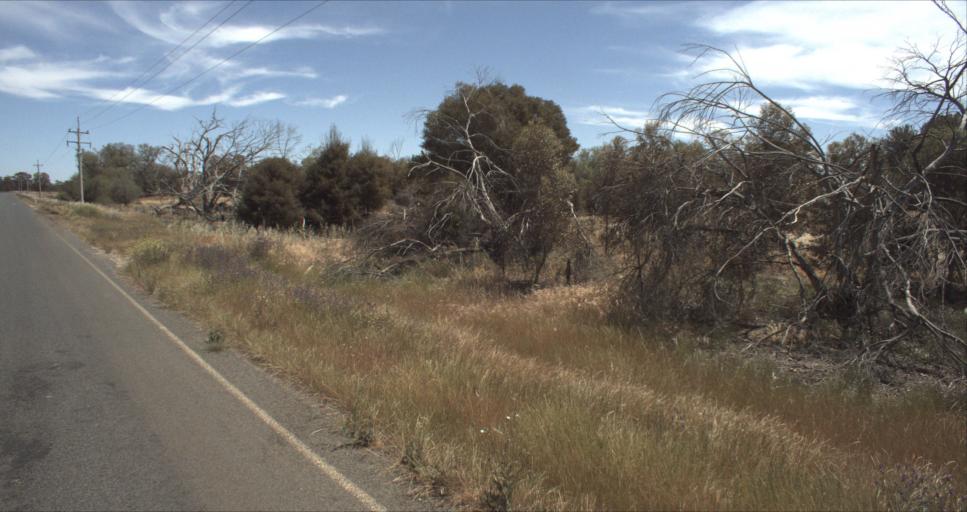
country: AU
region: New South Wales
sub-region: Leeton
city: Leeton
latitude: -34.6498
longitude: 146.4678
